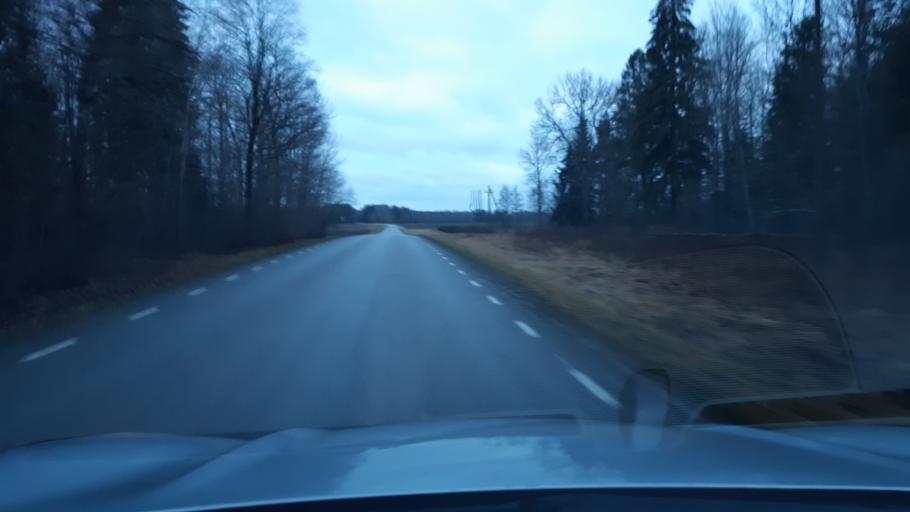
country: EE
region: Raplamaa
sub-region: Rapla vald
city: Rapla
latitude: 59.0381
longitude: 24.6773
